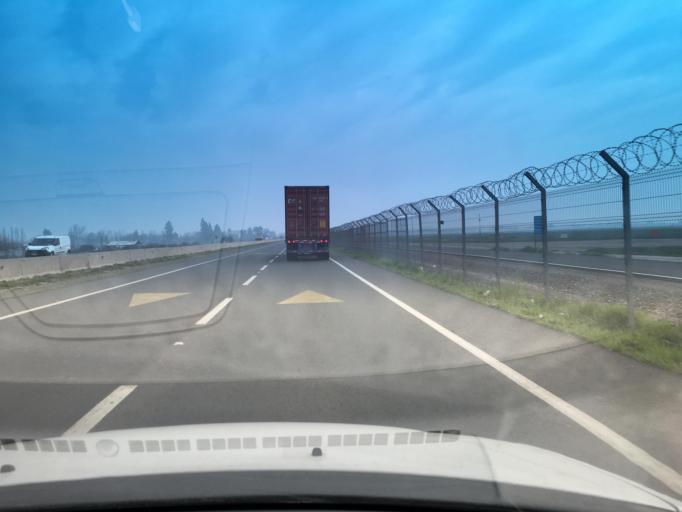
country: CL
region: Santiago Metropolitan
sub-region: Provincia de Santiago
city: Lo Prado
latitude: -33.3752
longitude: -70.8052
